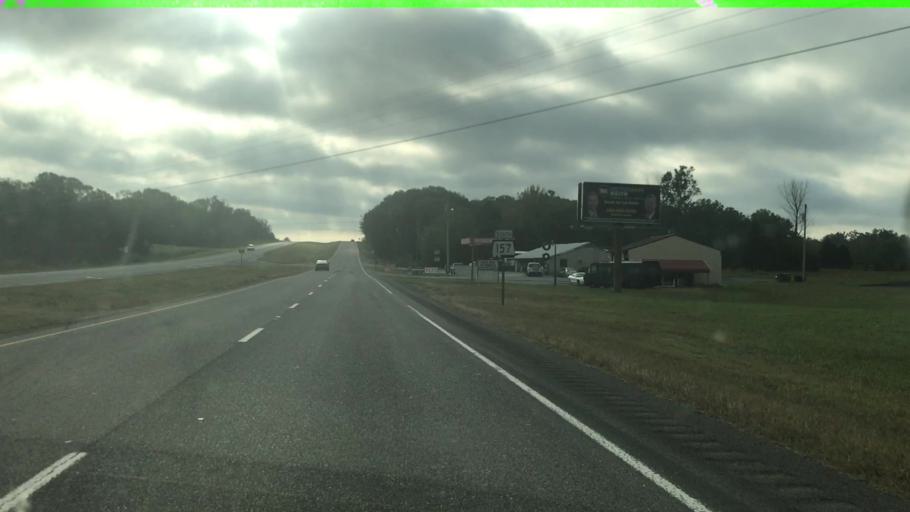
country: US
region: Alabama
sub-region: Morgan County
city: Danville
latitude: 34.4165
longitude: -87.1614
